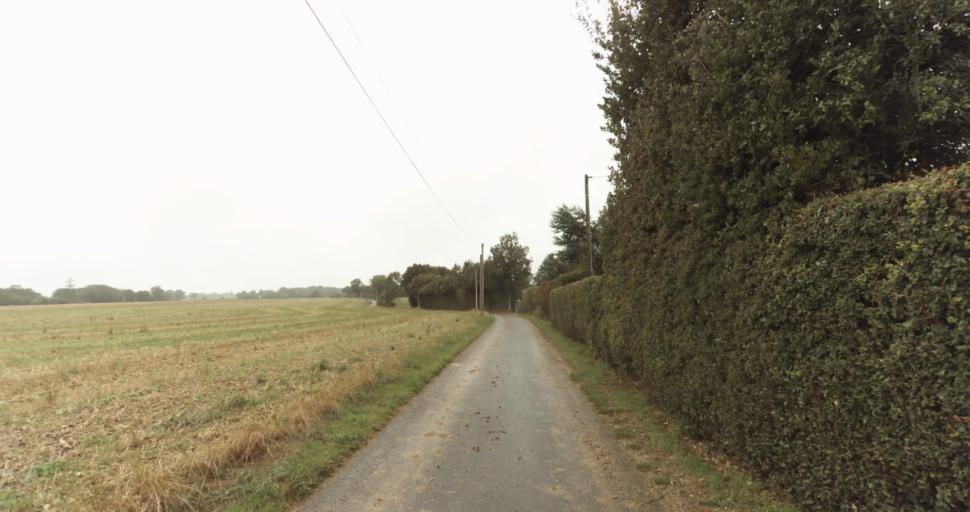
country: FR
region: Lower Normandy
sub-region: Departement de l'Orne
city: Vimoutiers
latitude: 48.8628
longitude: 0.2079
